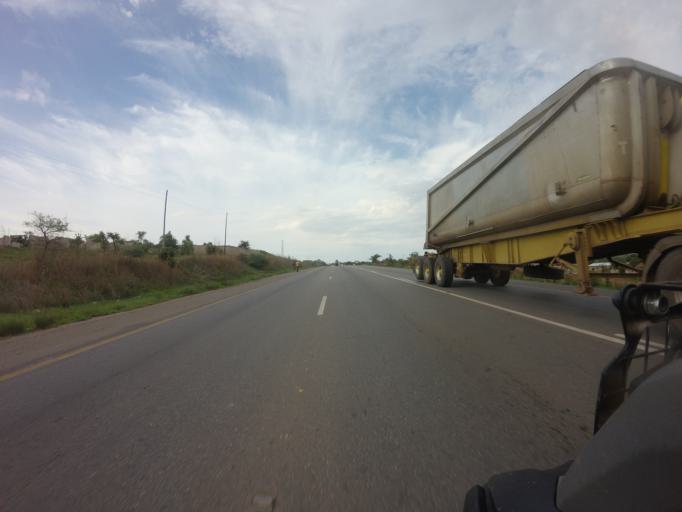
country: ZM
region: Lusaka
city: Lusaka
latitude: -15.5909
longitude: 28.2704
